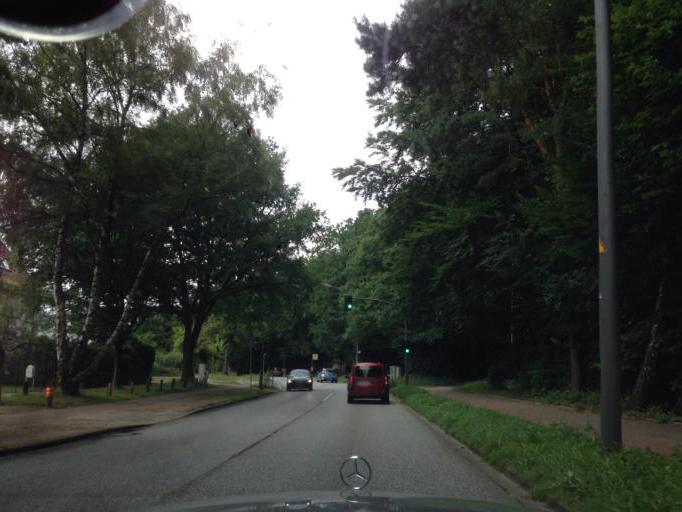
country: DE
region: Hamburg
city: Sasel
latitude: 53.6352
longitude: 10.1029
